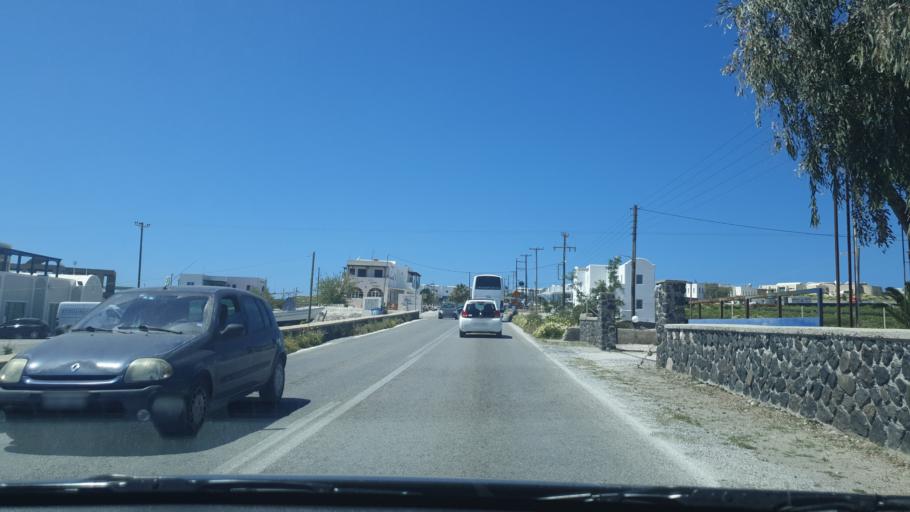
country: GR
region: South Aegean
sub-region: Nomos Kykladon
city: Emporeio
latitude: 36.3659
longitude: 25.4286
